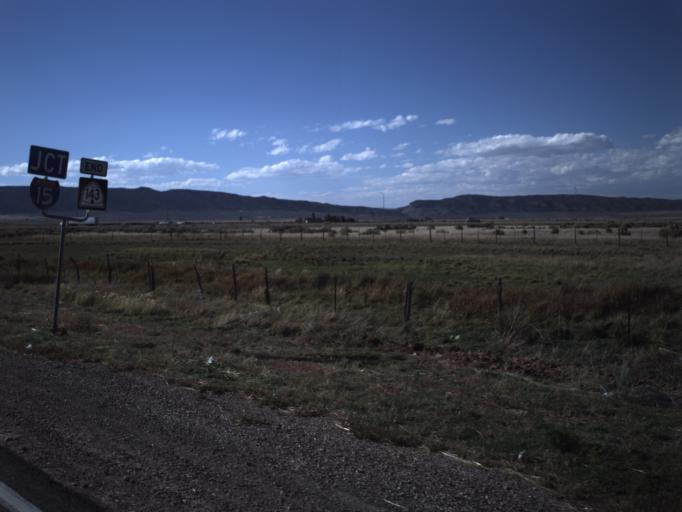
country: US
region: Utah
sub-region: Iron County
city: Parowan
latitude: 37.8385
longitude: -112.8633
